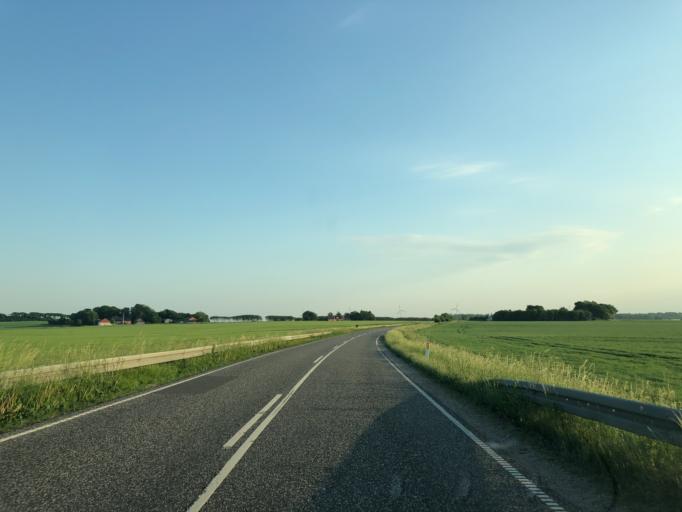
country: DK
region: Central Jutland
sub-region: Struer Kommune
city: Struer
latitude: 56.4434
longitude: 8.5325
